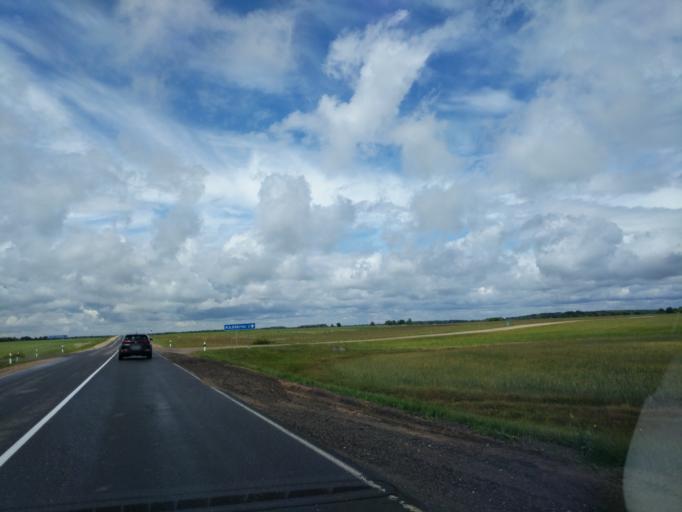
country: BY
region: Minsk
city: Il'ya
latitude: 54.3884
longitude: 27.3550
